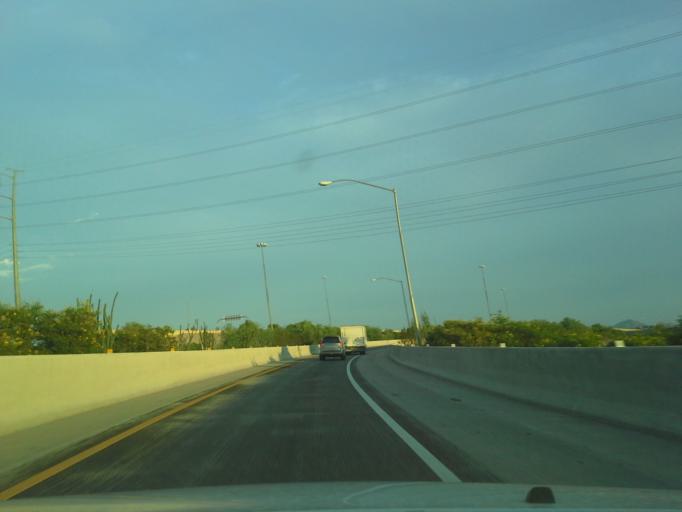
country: US
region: Arizona
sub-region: Maricopa County
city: Paradise Valley
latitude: 33.6706
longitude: -112.0019
